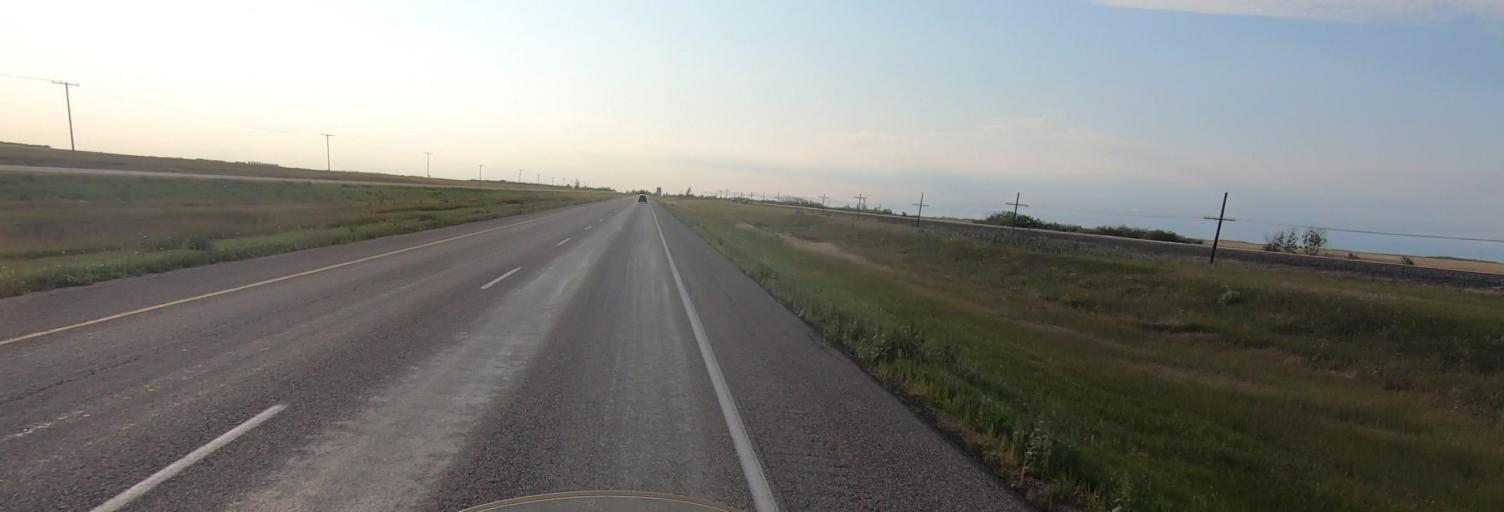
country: CA
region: Saskatchewan
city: Indian Head
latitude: 50.4657
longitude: -103.4135
